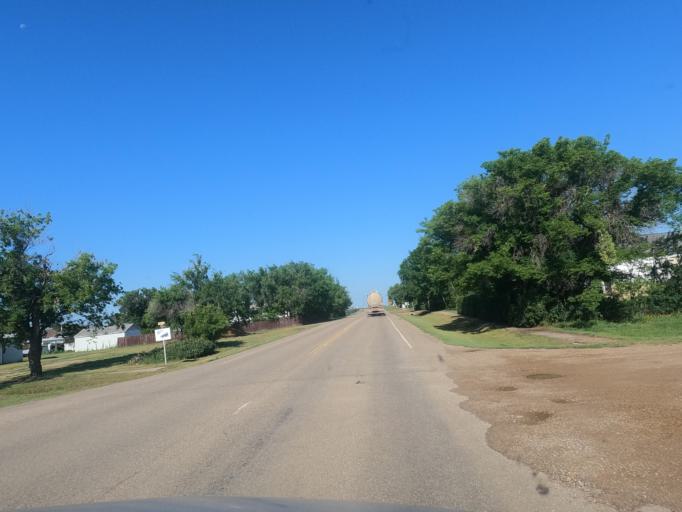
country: CA
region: Saskatchewan
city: Swift Current
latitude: 49.7278
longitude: -107.7393
